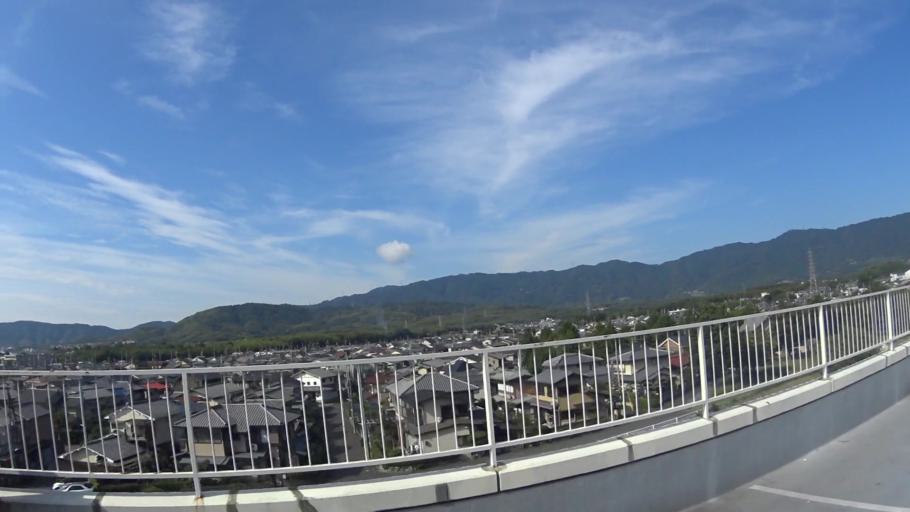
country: JP
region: Kyoto
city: Muko
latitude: 34.9494
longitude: 135.6924
